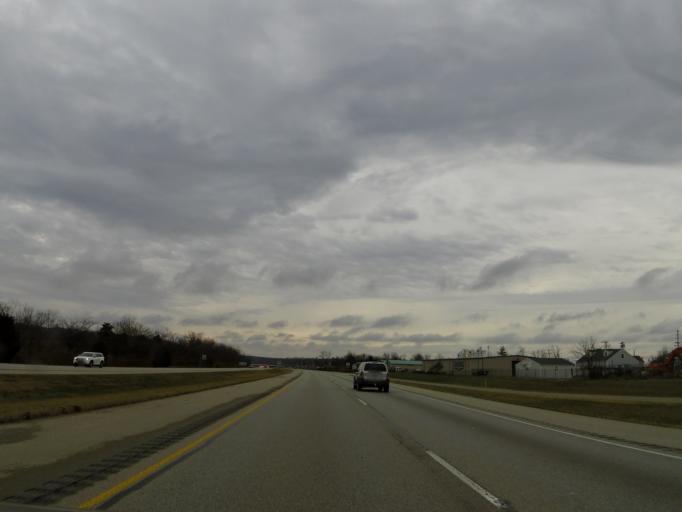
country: US
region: Ohio
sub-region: Hamilton County
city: Harrison
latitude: 39.2472
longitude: -84.7832
